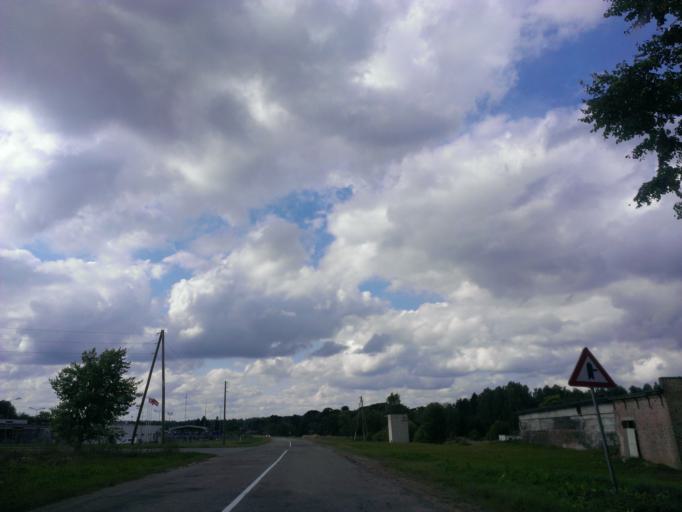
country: LV
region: Ropazu
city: Ropazi
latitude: 56.9654
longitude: 24.5203
